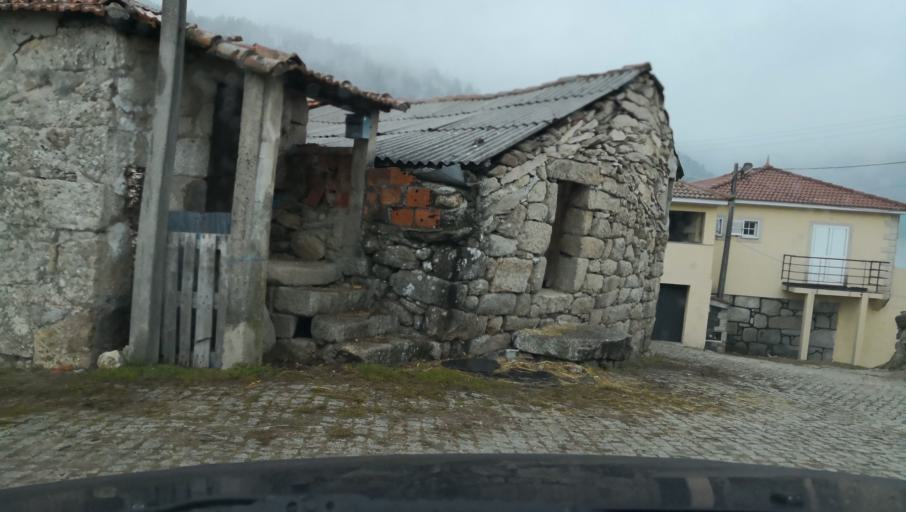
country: PT
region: Vila Real
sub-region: Vila Real
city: Vila Real
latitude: 41.3333
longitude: -7.7831
